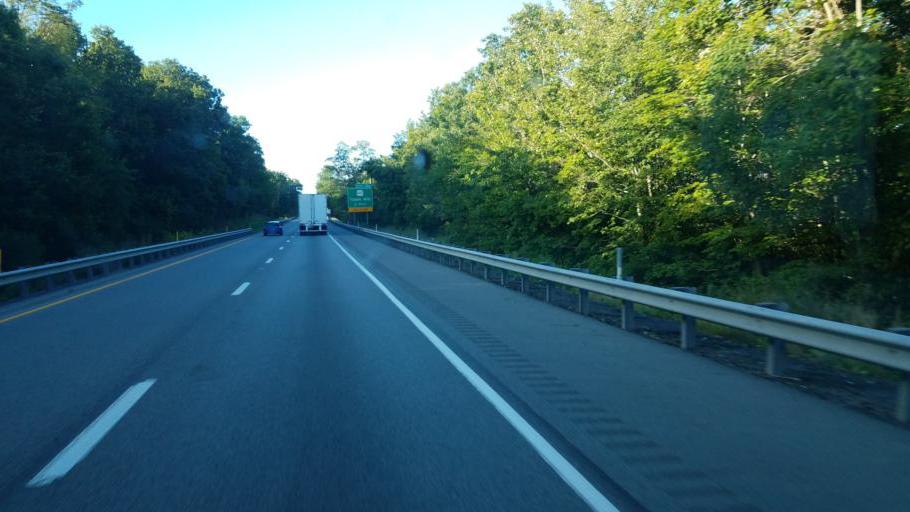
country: US
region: Pennsylvania
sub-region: Bedford County
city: Earlston
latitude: 39.9167
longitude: -78.2360
